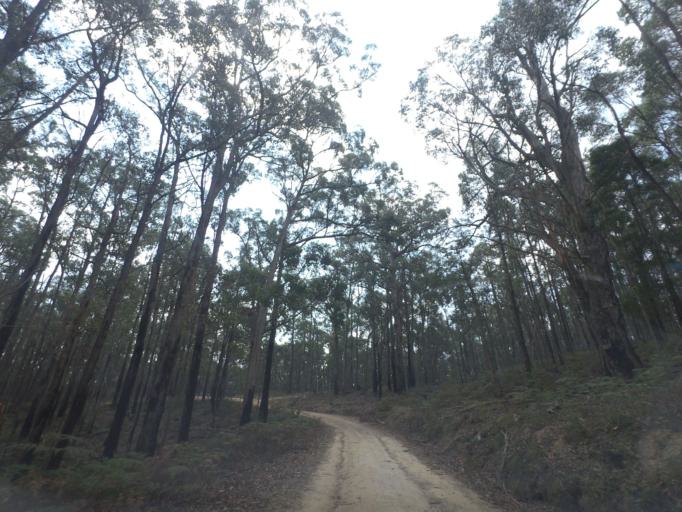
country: AU
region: Victoria
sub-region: Moorabool
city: Bacchus Marsh
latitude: -37.4658
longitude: 144.3869
